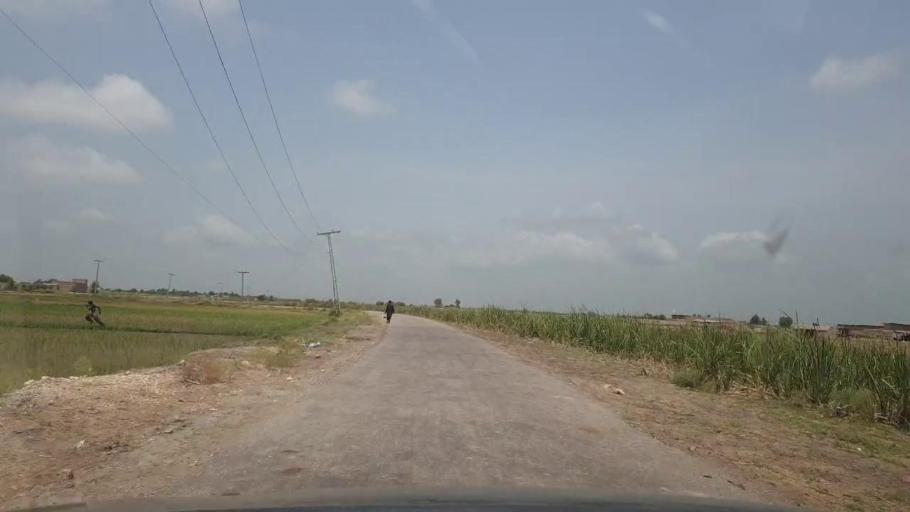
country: PK
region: Sindh
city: Ratodero
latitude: 27.9030
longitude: 68.3193
